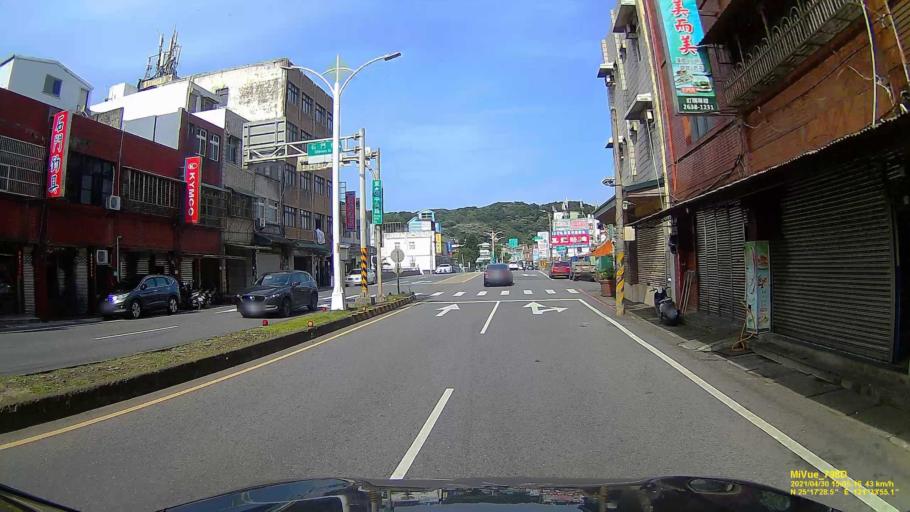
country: TW
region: Taiwan
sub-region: Keelung
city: Keelung
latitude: 25.2913
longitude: 121.5655
